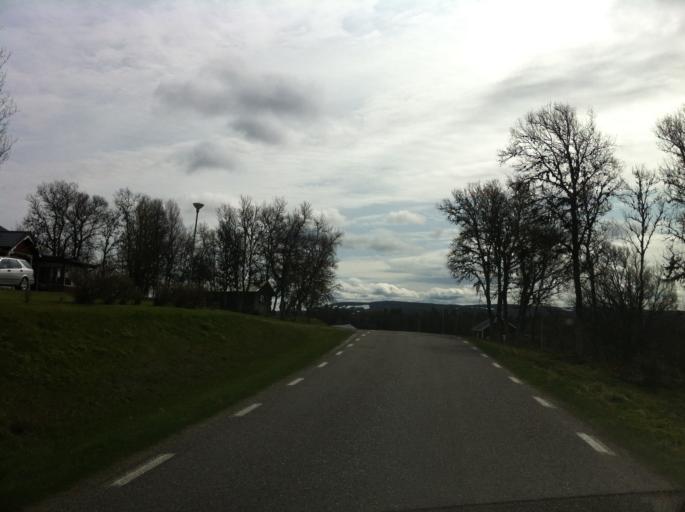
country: NO
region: Hedmark
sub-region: Engerdal
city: Engerdal
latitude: 62.2960
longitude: 12.8080
